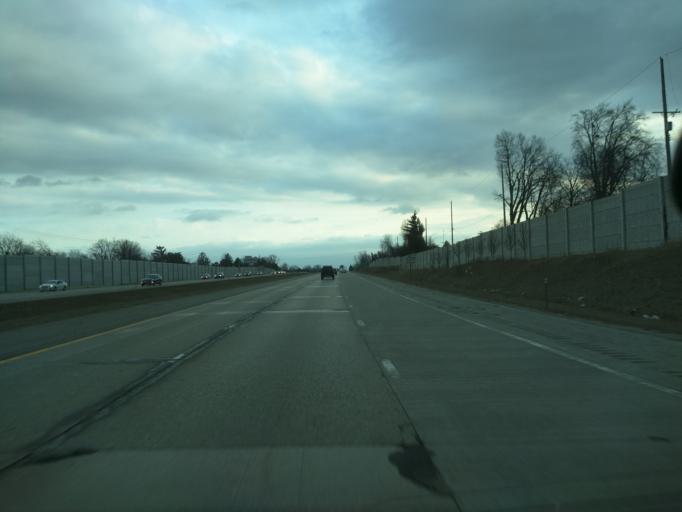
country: US
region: Michigan
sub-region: Ingham County
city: East Lansing
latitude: 42.7549
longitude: -84.5080
